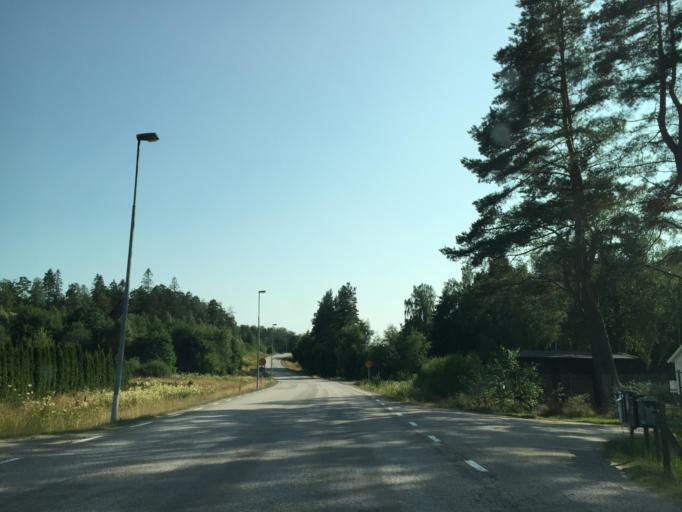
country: SE
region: Vaestra Goetaland
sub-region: Trollhattan
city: Trollhattan
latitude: 58.3295
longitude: 12.2639
